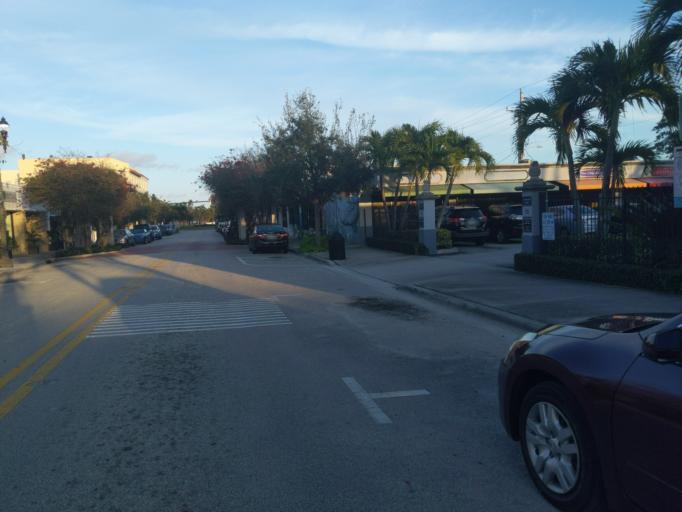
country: US
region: Florida
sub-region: Palm Beach County
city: West Palm Beach
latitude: 26.7350
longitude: -80.0542
